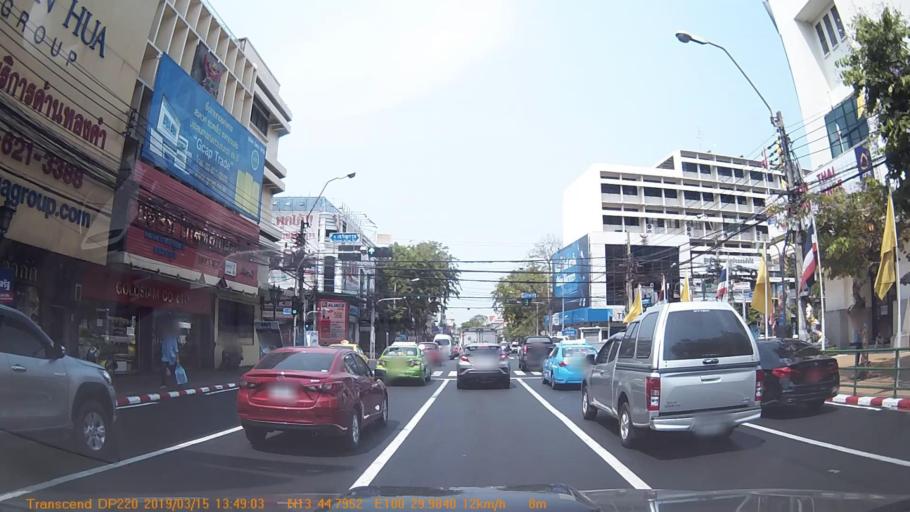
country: TH
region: Bangkok
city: Bangkok
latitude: 13.7466
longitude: 100.4998
